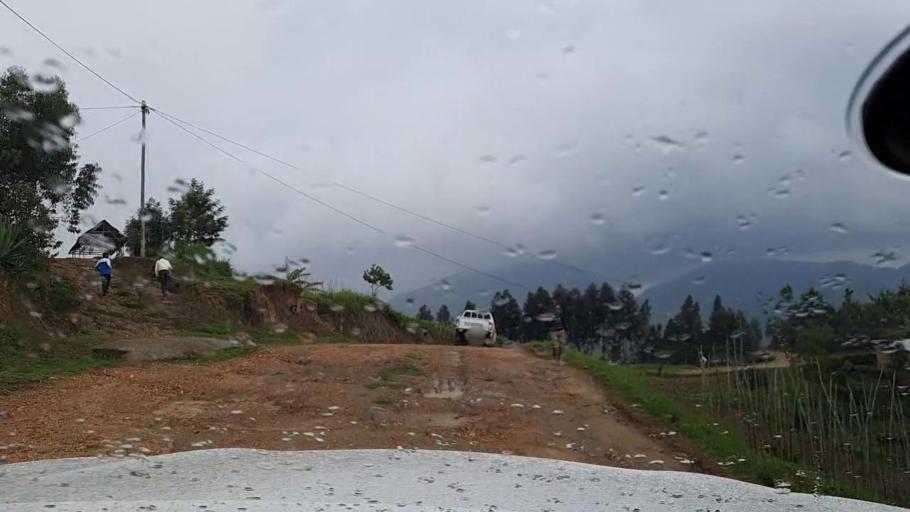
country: RW
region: Western Province
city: Kibuye
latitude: -2.1103
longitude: 29.4838
